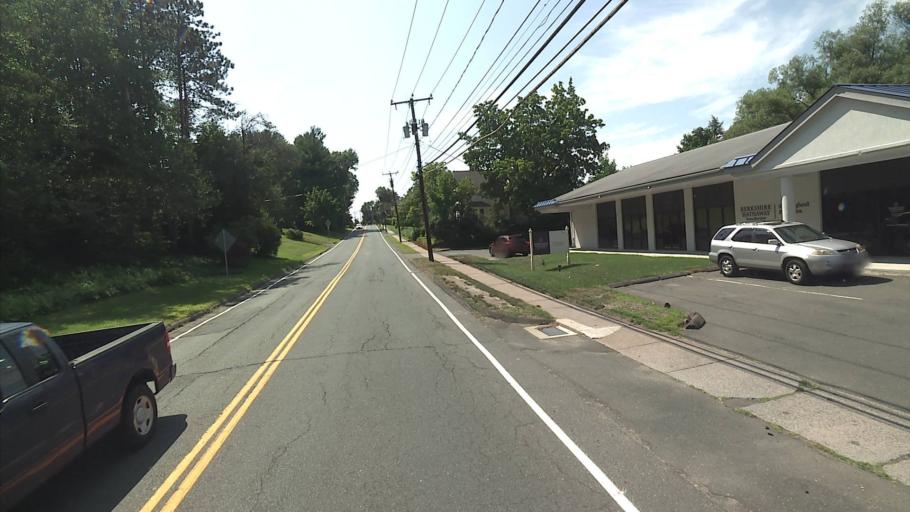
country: US
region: Connecticut
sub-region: Hartford County
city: Windsor
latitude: 41.8522
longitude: -72.6538
